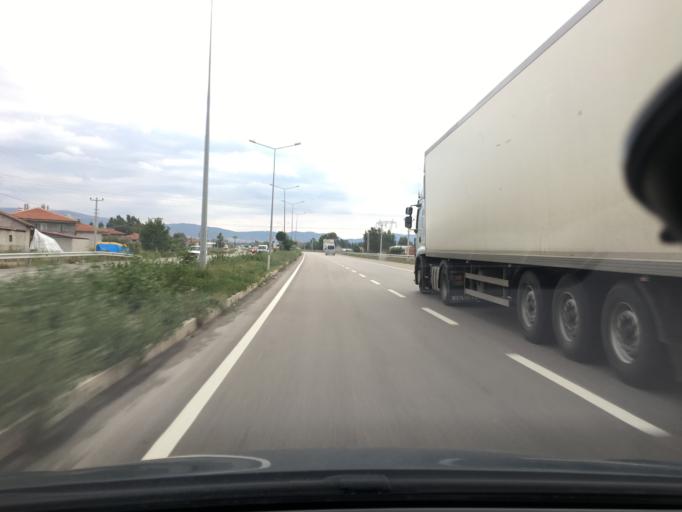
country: TR
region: Afyonkarahisar
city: Sincanli
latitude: 38.7885
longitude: 30.3796
